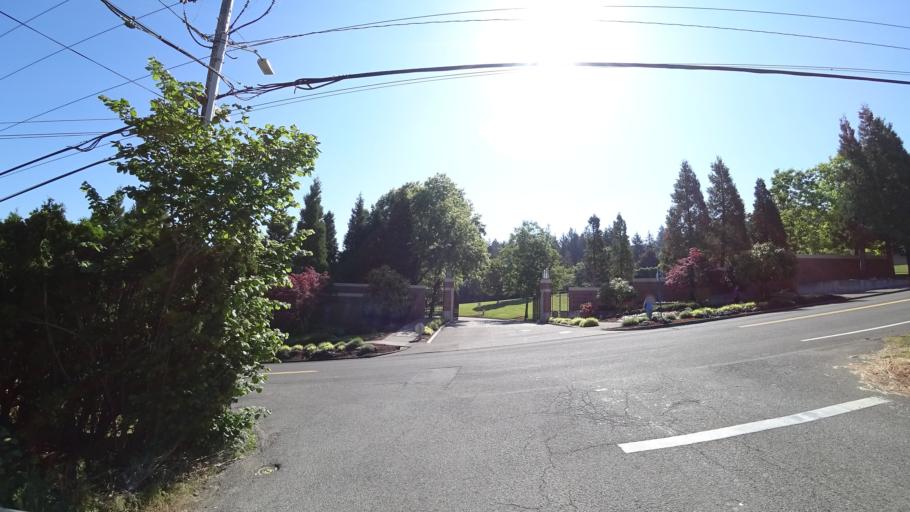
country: US
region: Oregon
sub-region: Multnomah County
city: Lents
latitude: 45.4647
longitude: -122.5483
